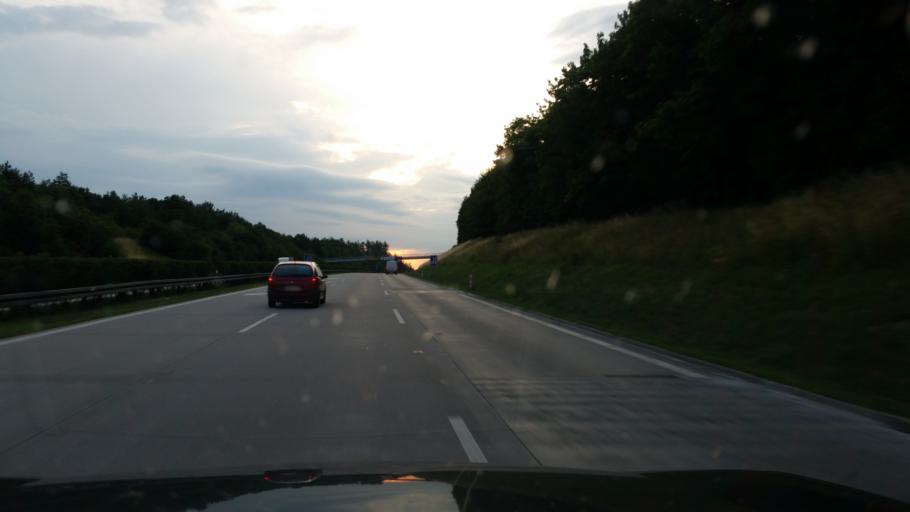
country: CZ
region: Olomoucky
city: Dolni Ujezd
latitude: 49.5597
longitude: 17.5147
